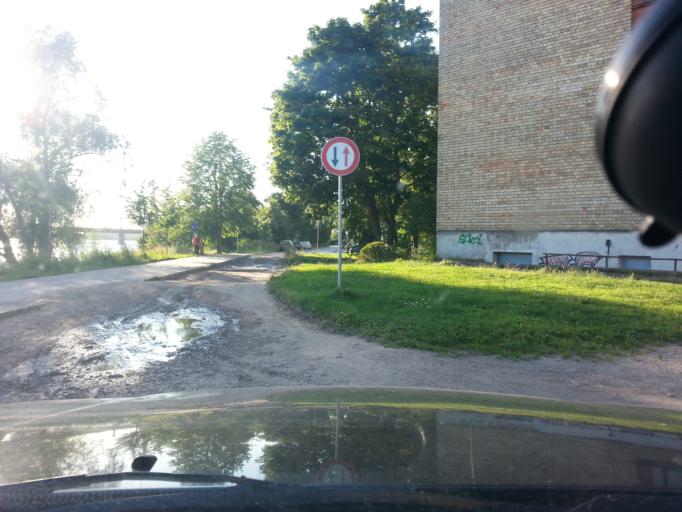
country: LV
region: Kekava
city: Balozi
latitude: 56.9147
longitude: 24.1673
